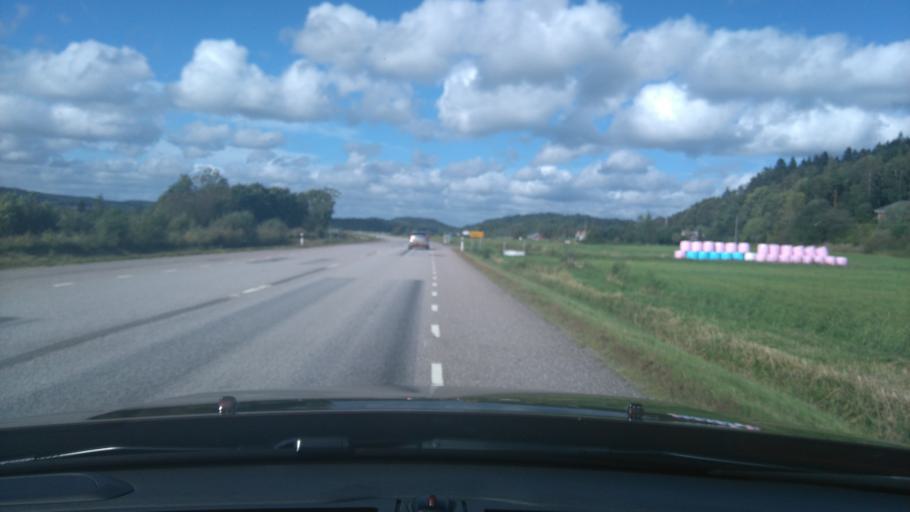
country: SE
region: Vaestra Goetaland
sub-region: Lilla Edets Kommun
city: Lodose
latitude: 58.0443
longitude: 12.1508
